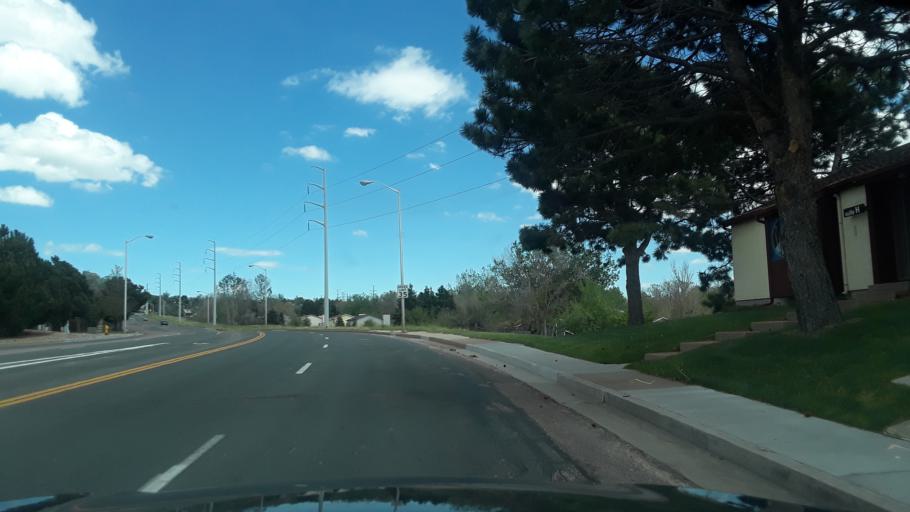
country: US
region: Colorado
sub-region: El Paso County
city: Air Force Academy
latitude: 38.9443
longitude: -104.7921
